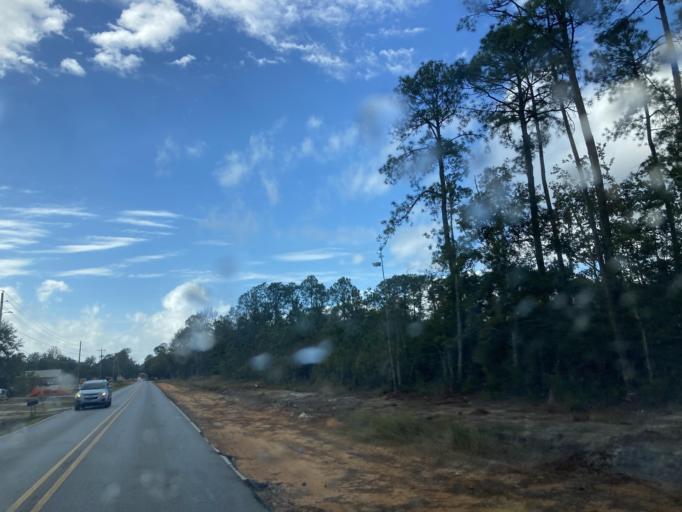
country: US
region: Mississippi
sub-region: Jackson County
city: Gulf Hills
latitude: 30.4391
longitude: -88.8271
